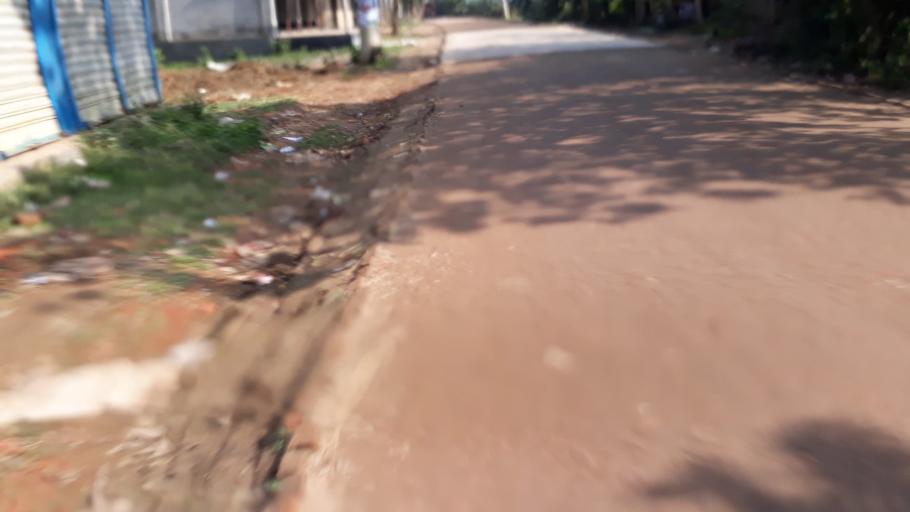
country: BD
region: Dhaka
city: Tungi
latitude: 23.8555
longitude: 90.3051
